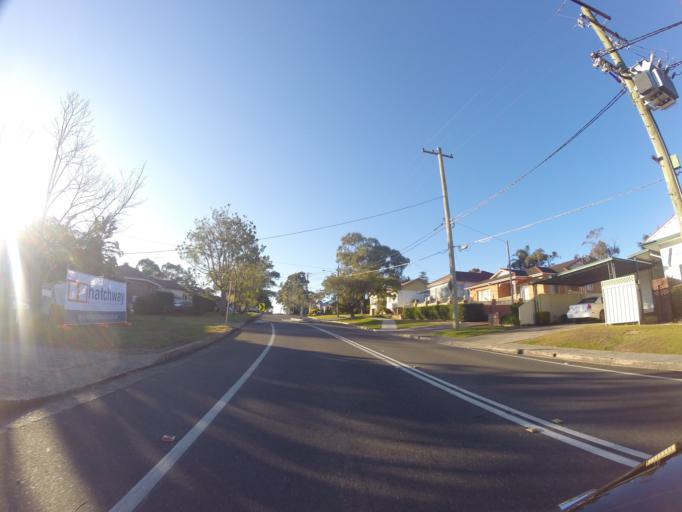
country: AU
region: New South Wales
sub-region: Sutherland Shire
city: Gymea
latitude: -34.0445
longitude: 151.0801
